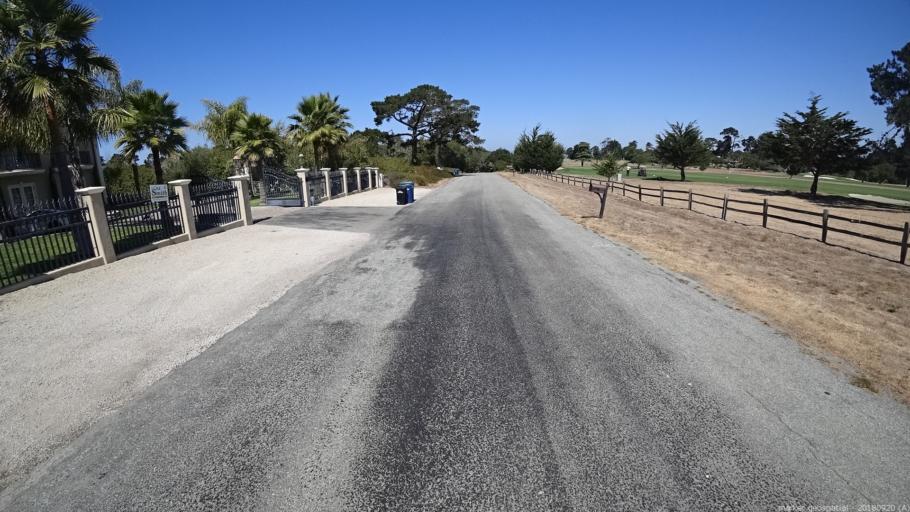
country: US
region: California
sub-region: Monterey County
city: Monterey
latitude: 36.5804
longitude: -121.8716
